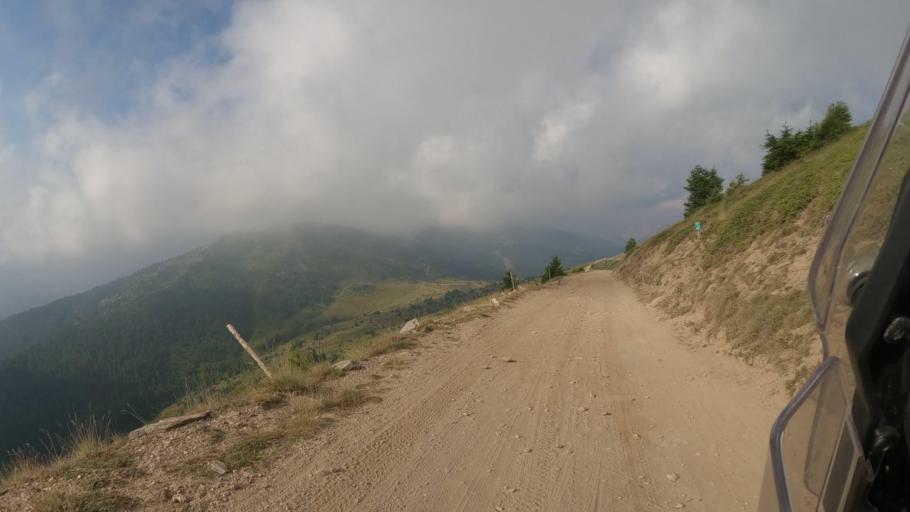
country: IT
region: Piedmont
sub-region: Provincia di Torino
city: Pragelato-Rua
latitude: 45.0315
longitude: 6.9076
